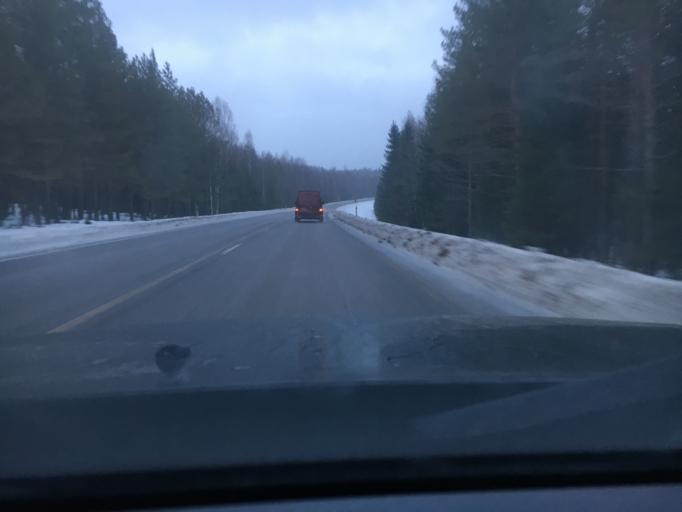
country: FI
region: Central Finland
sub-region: Jyvaeskylae
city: Hankasalmi
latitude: 62.4121
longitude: 26.6916
